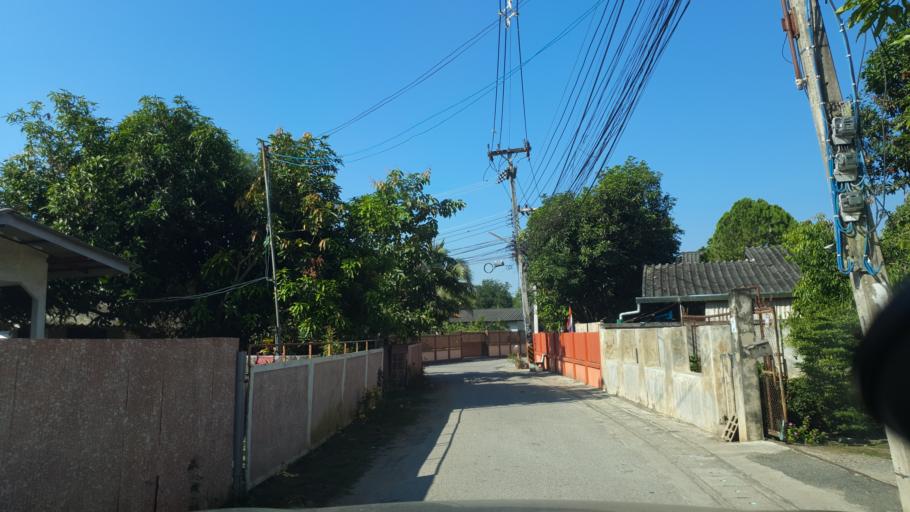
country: TH
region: Chiang Mai
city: San Kamphaeng
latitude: 18.7342
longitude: 99.1385
